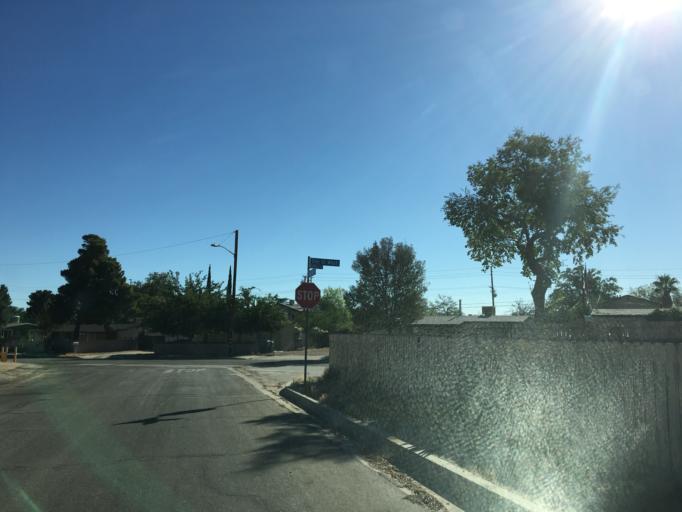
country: US
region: California
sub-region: Los Angeles County
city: Desert View Highlands
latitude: 34.5902
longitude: -118.1494
